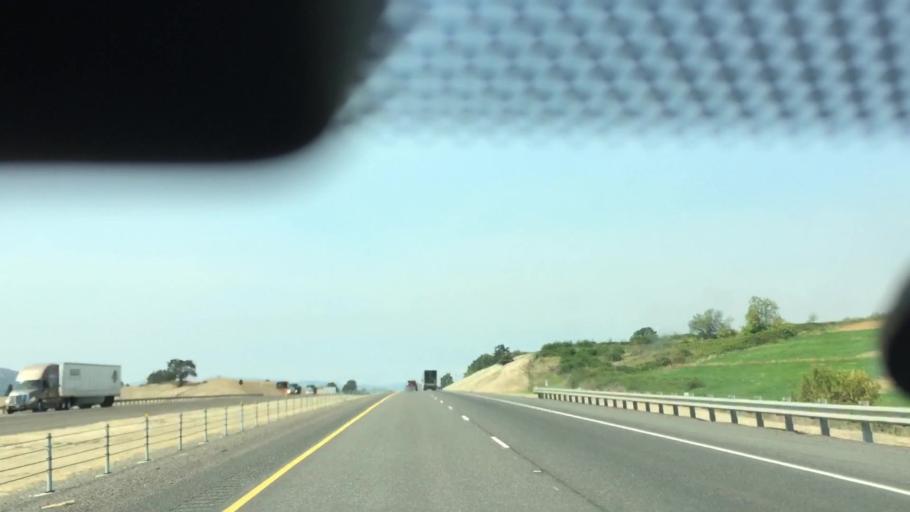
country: US
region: Oregon
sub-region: Jackson County
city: Ashland
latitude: 42.2029
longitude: -122.6858
